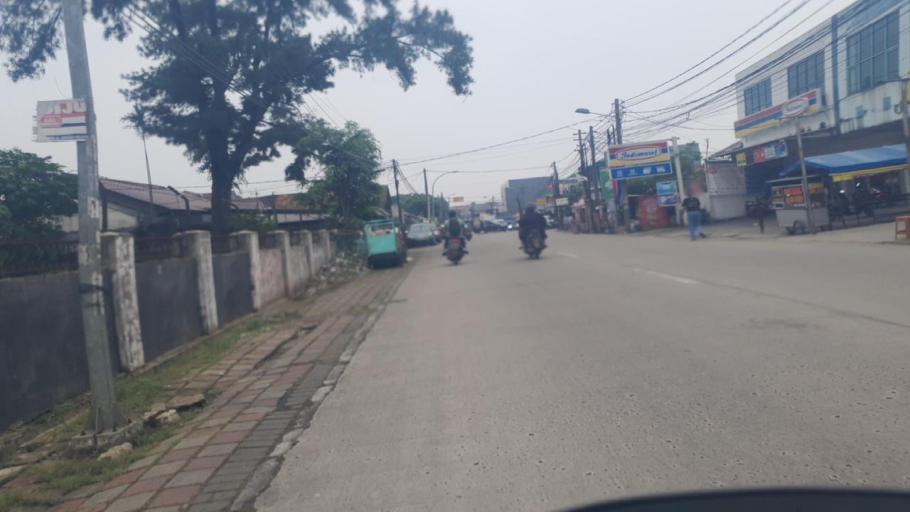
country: ID
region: West Java
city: Bogor
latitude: -6.5853
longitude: 106.7877
